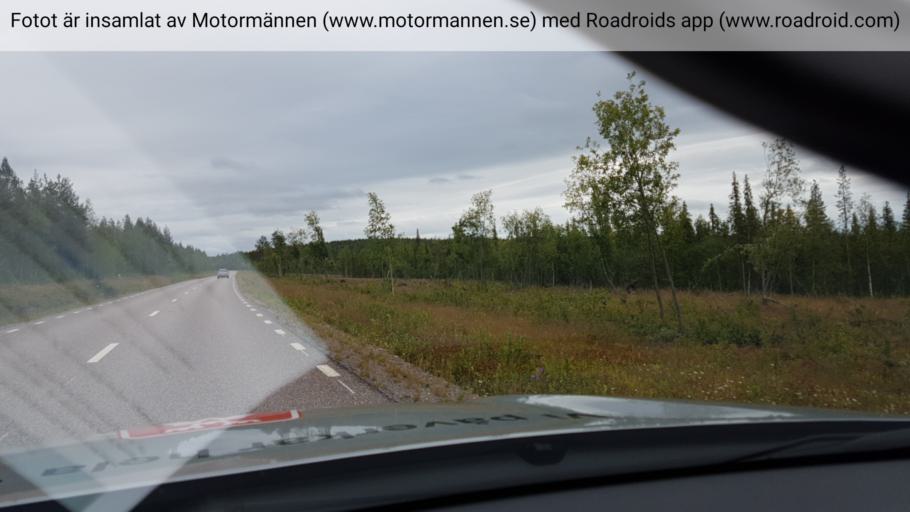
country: SE
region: Norrbotten
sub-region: Gallivare Kommun
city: Gaellivare
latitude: 67.0417
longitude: 21.6457
